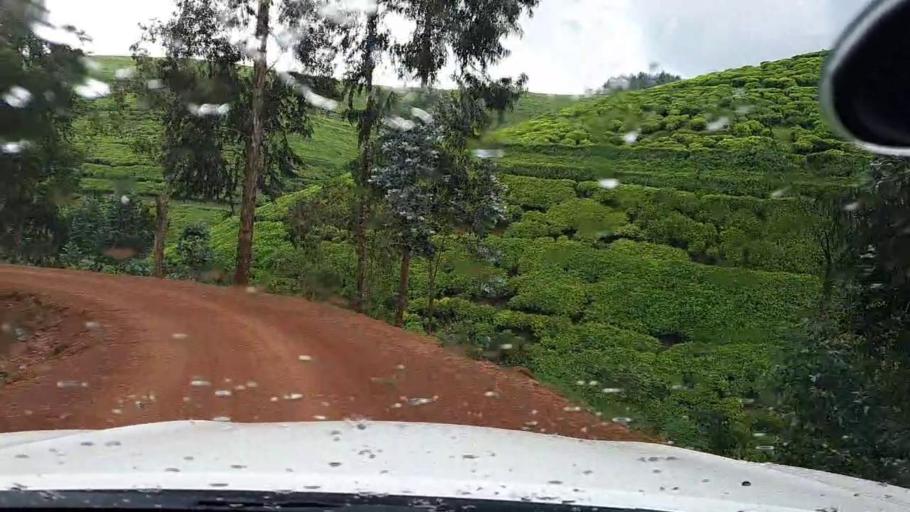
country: RW
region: Western Province
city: Kibuye
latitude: -2.1685
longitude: 29.4365
